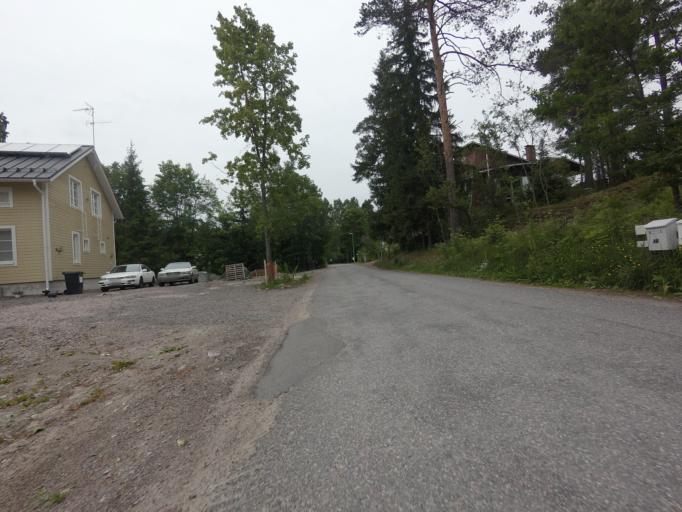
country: FI
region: Uusimaa
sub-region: Helsinki
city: Kauniainen
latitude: 60.1882
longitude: 24.7270
